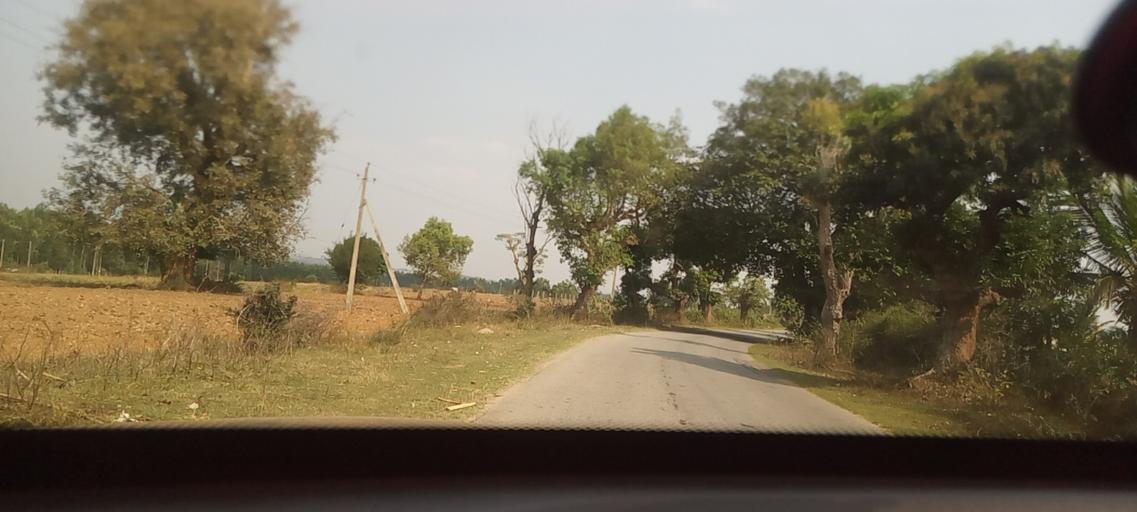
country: IN
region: Karnataka
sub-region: Hassan
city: Belur
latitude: 13.1817
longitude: 75.8411
